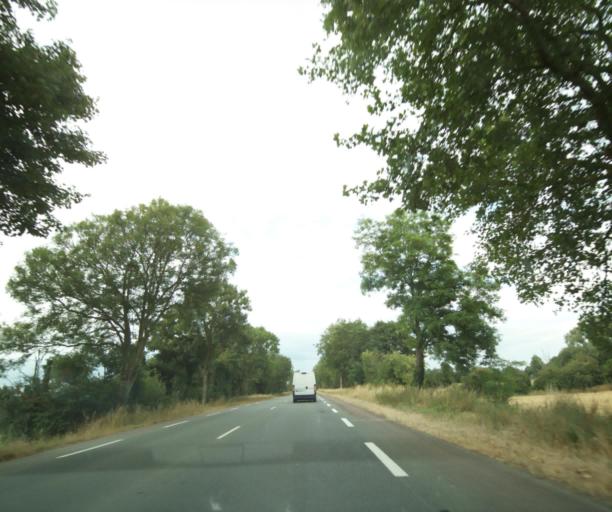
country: FR
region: Poitou-Charentes
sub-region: Departement de la Charente-Maritime
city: Marans
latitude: 46.2763
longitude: -0.9996
